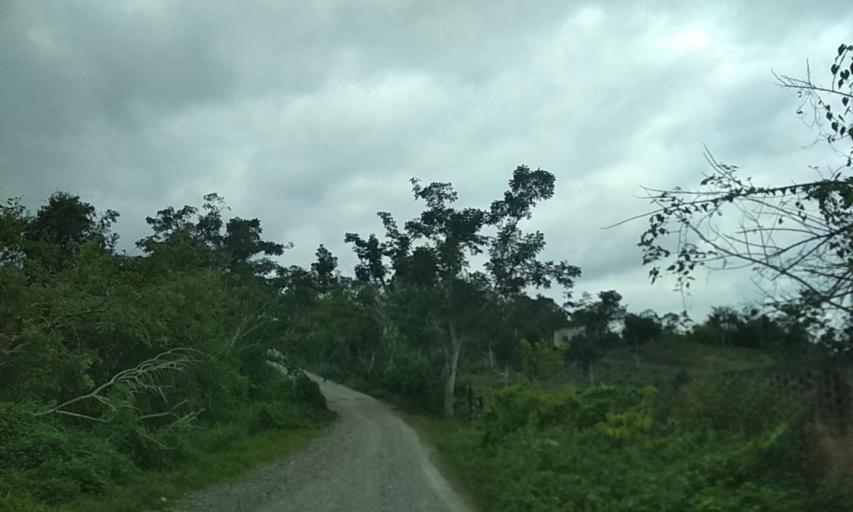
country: MX
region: Veracruz
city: Papantla de Olarte
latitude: 20.4763
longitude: -97.3095
